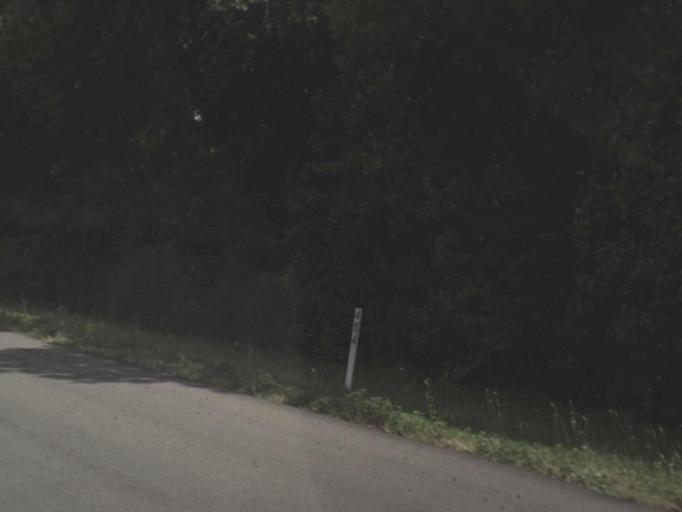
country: US
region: Georgia
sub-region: Camden County
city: Kingsland
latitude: 30.7023
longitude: -81.6757
